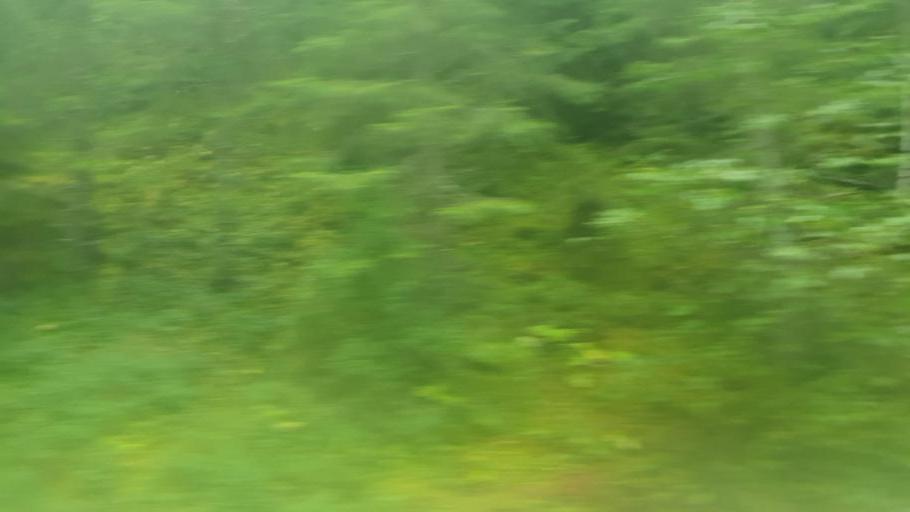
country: NO
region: Nord-Trondelag
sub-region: Levanger
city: Skogn
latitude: 63.6181
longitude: 11.2186
